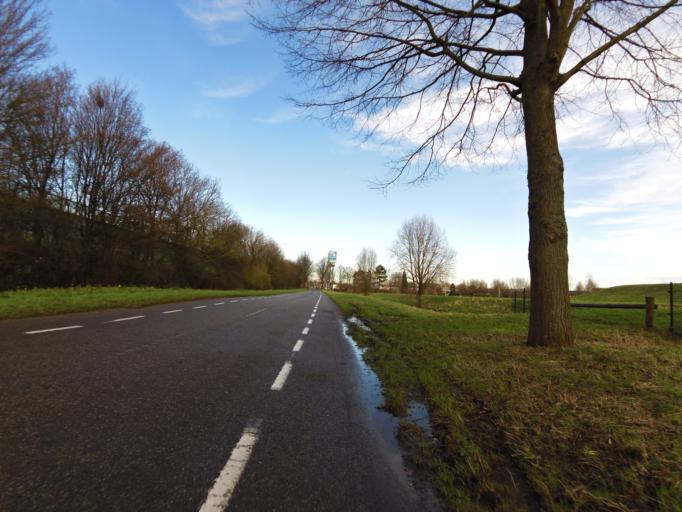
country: NL
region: South Holland
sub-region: Gemeente Delft
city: Delft
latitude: 52.0021
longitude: 4.3874
